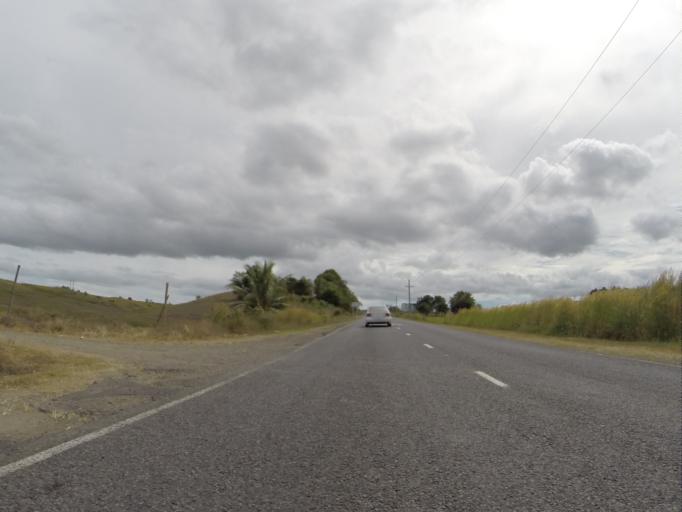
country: FJ
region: Western
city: Nadi
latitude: -18.0370
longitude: 177.3351
